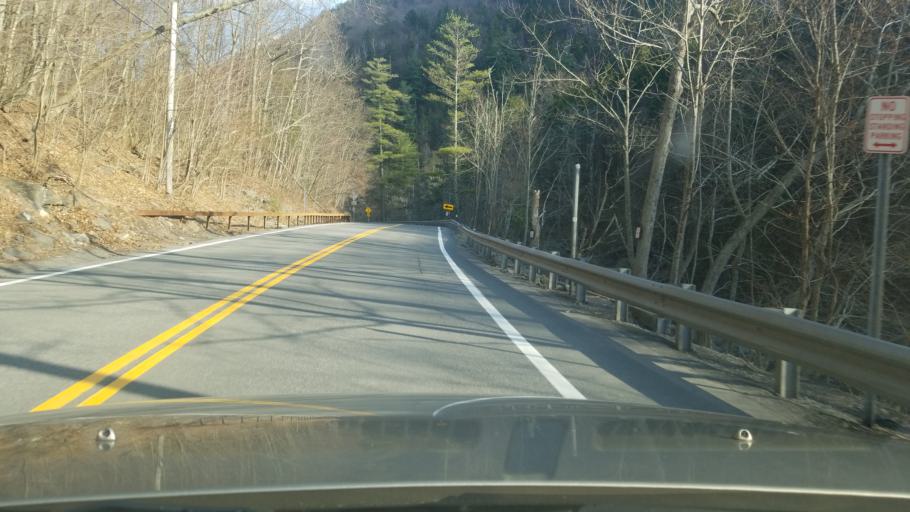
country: US
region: New York
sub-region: Greene County
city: Palenville
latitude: 42.1781
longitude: -74.0586
